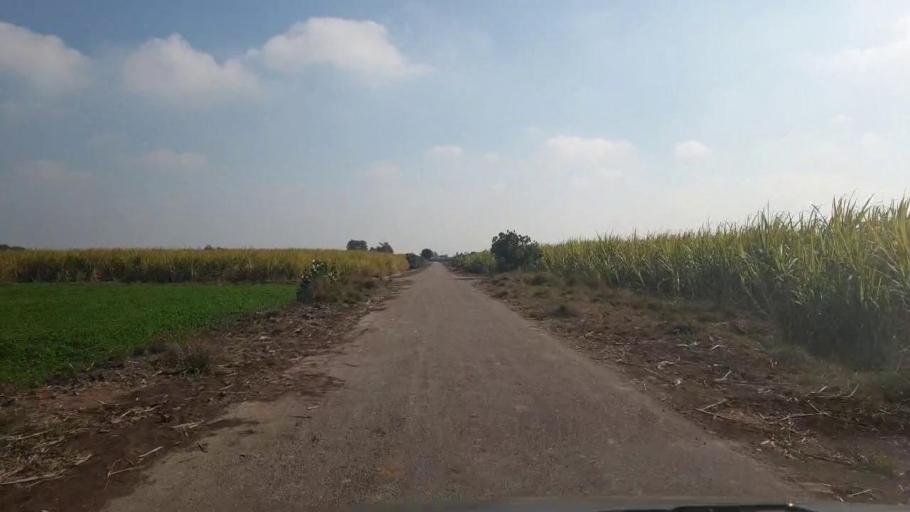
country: PK
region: Sindh
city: Shahdadpur
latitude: 25.8924
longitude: 68.5923
